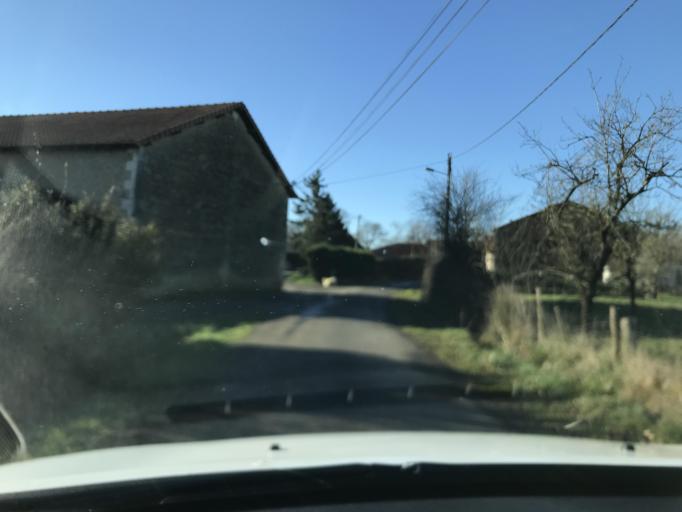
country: FR
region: Poitou-Charentes
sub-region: Departement de la Charente
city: Loubert
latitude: 45.8407
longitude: 0.5370
